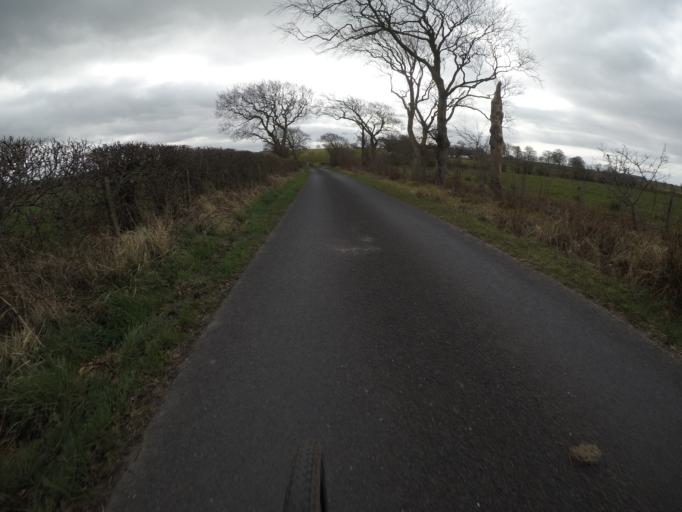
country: GB
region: Scotland
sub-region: North Ayrshire
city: Springside
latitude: 55.6648
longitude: -4.5913
